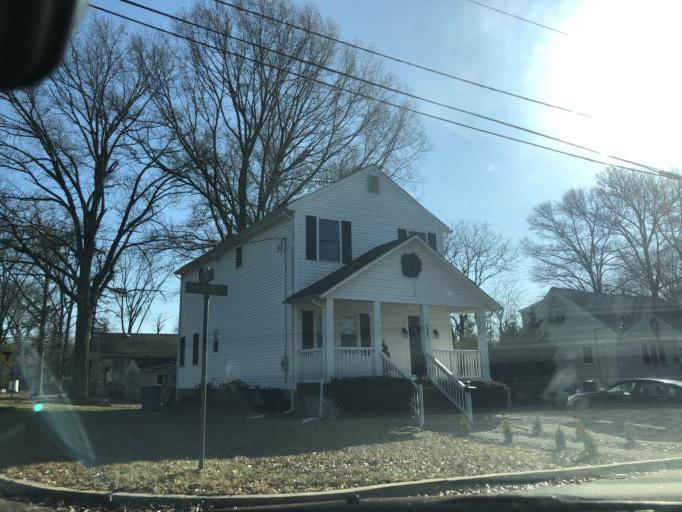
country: US
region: New Jersey
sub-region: Burlington County
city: Moorestown-Lenola
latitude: 39.9626
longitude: -74.9778
